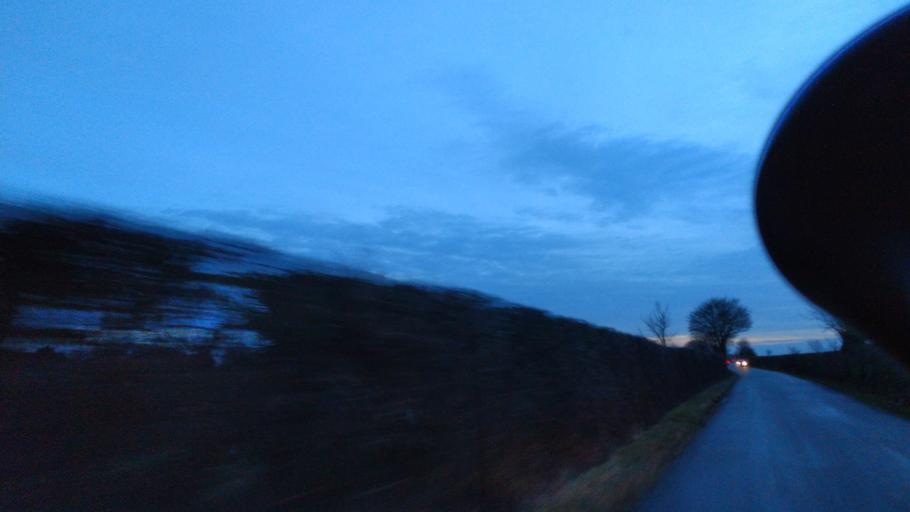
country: GB
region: England
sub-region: Borough of Swindon
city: Highworth
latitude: 51.6078
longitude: -1.7248
